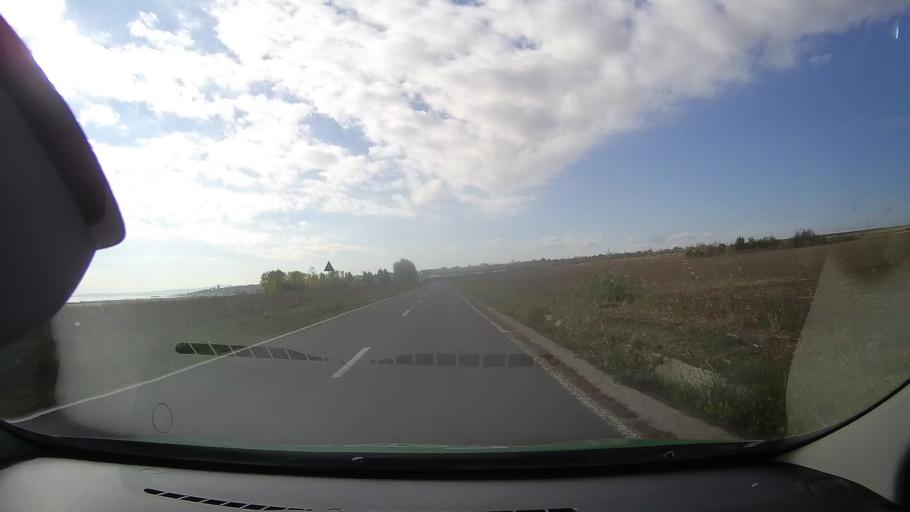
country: RO
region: Tulcea
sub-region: Comuna Sarichioi
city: Sarichioi
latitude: 44.9610
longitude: 28.8599
